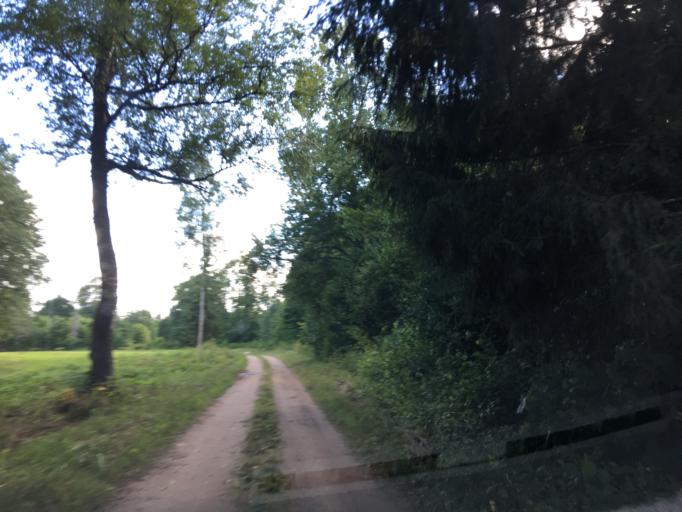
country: EE
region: Viljandimaa
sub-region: Suure-Jaani vald
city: Suure-Jaani
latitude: 58.4954
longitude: 25.2598
